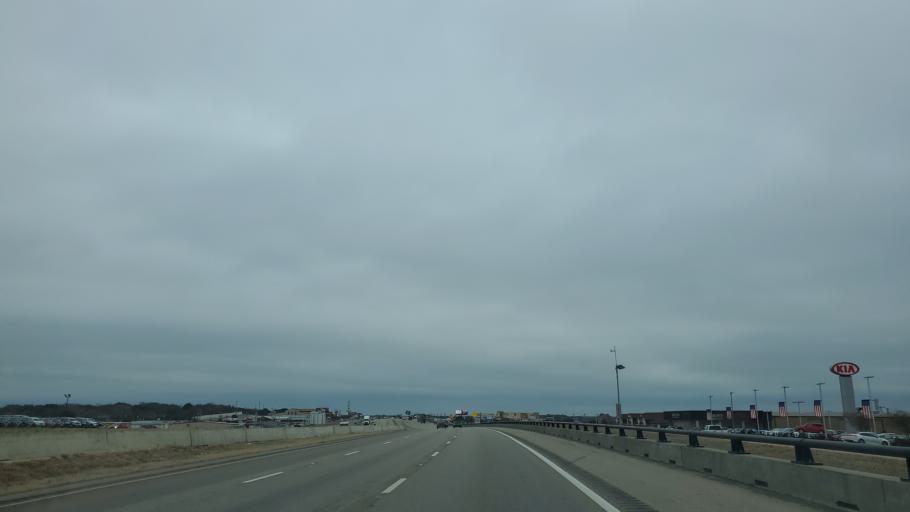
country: US
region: Texas
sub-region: Bell County
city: Harker Heights
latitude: 31.0777
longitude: -97.6934
